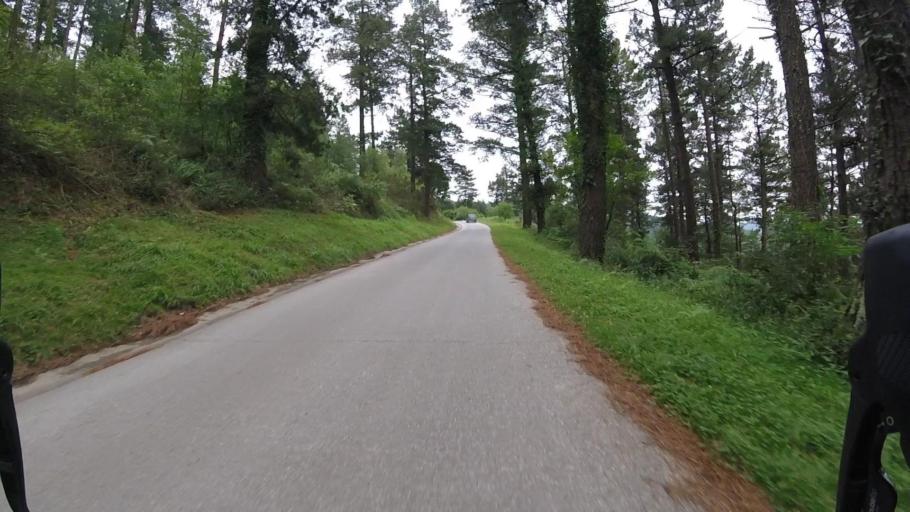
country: ES
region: Basque Country
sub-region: Provincia de Guipuzcoa
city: Errenteria
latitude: 43.2599
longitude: -1.8915
